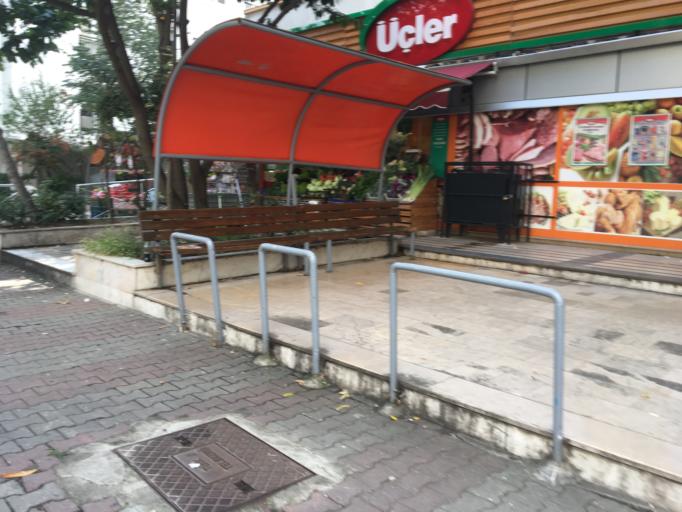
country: TR
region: Istanbul
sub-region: Atasehir
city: Atasehir
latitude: 40.9645
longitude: 29.0946
